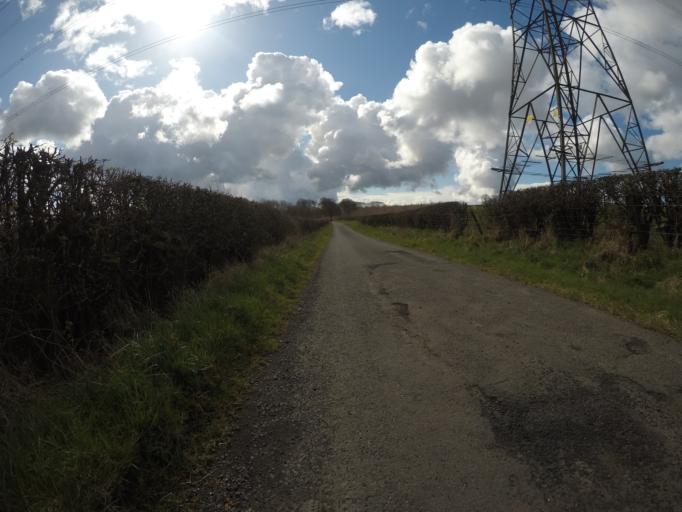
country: GB
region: Scotland
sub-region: North Ayrshire
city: Kilbirnie
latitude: 55.7299
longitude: -4.6700
